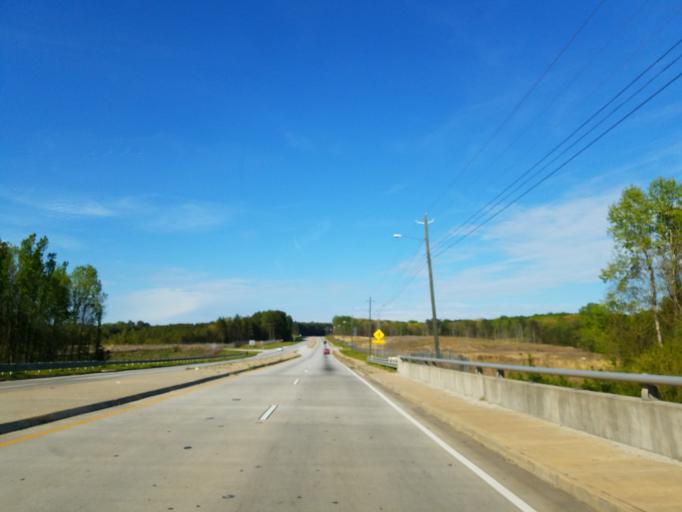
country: US
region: Georgia
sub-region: Cobb County
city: Mableton
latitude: 33.7816
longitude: -84.5087
